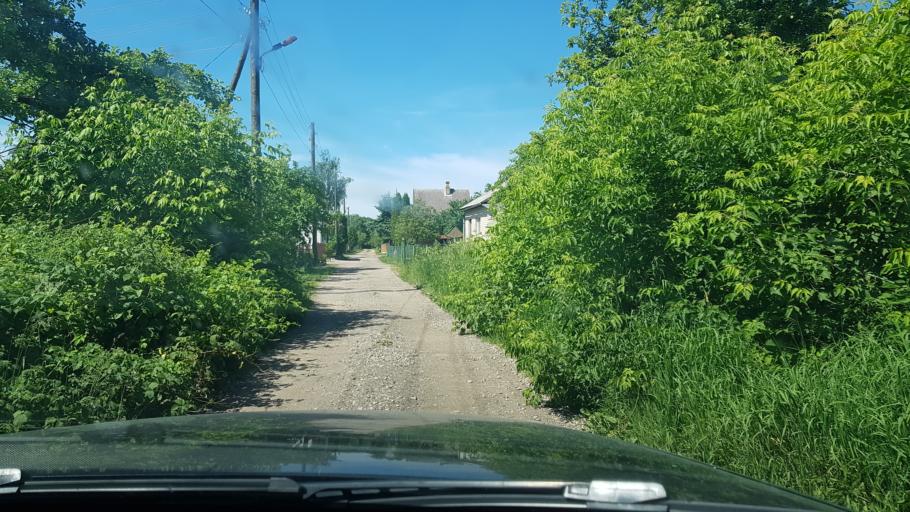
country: LV
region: Daugavpils
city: Daugavpils
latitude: 55.8604
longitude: 26.5704
